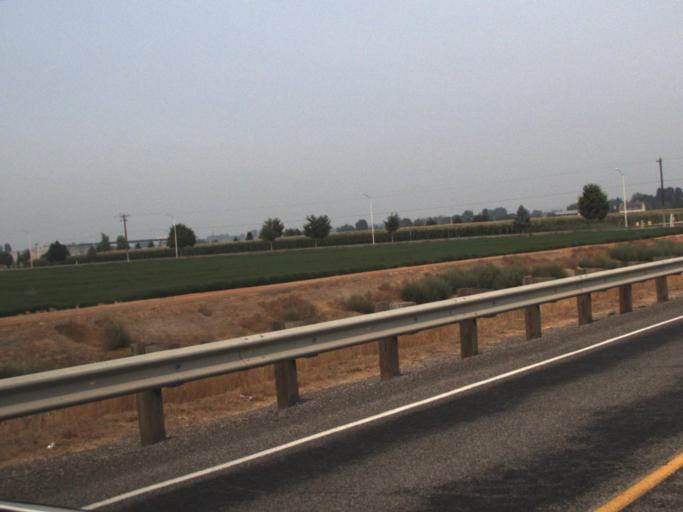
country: US
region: Washington
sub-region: Yakima County
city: Sunnyside
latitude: 46.3229
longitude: -119.9785
